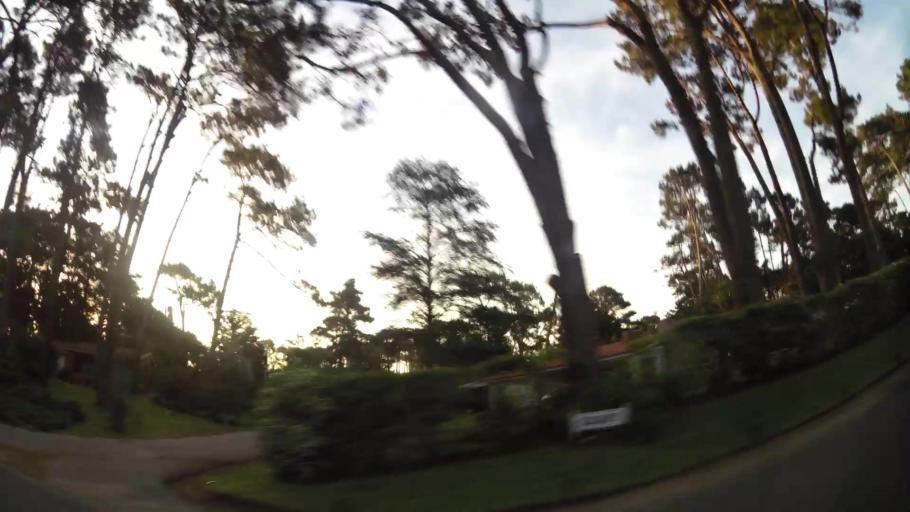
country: UY
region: Maldonado
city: Punta del Este
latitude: -34.9335
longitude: -54.9358
